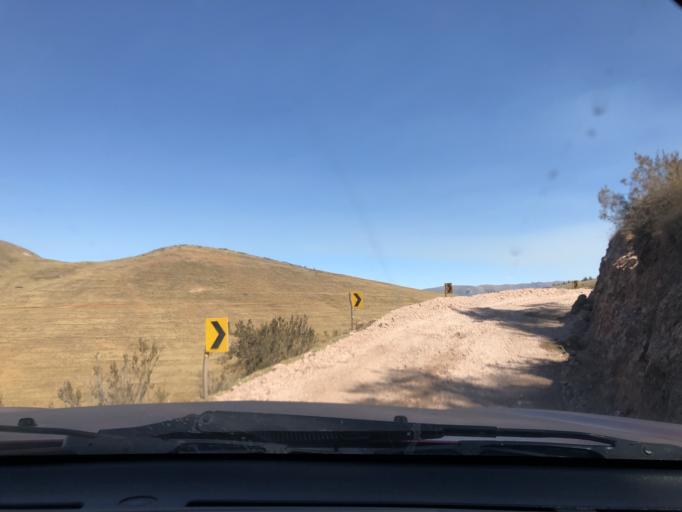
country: PE
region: Ayacucho
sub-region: Provincia de La Mar
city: Chilcas
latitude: -13.1828
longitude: -73.8404
